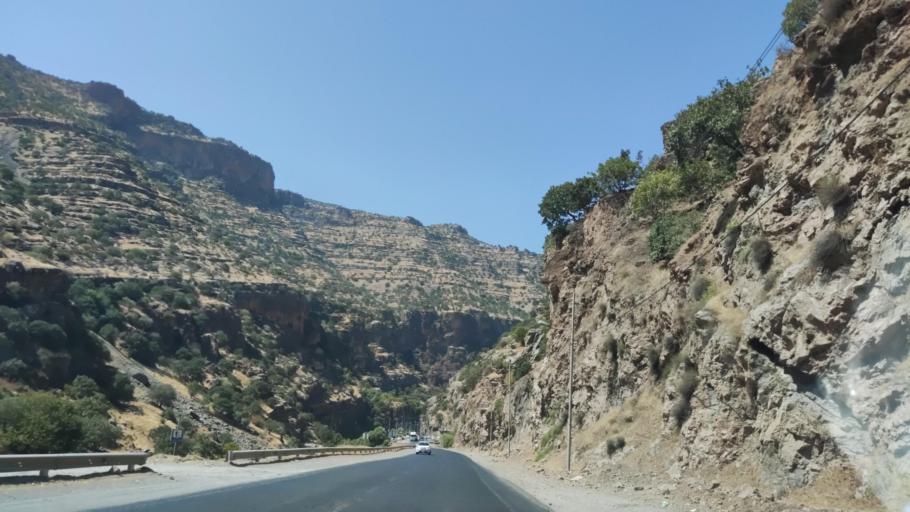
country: IQ
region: Arbil
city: Ruwandiz
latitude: 36.6299
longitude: 44.4730
